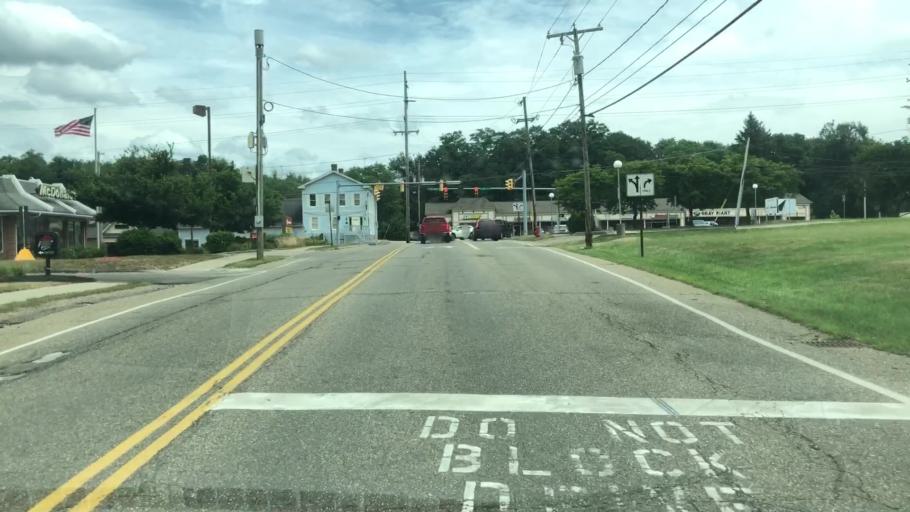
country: US
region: Ohio
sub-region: Summit County
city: Munroe Falls
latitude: 41.1394
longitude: -81.4404
